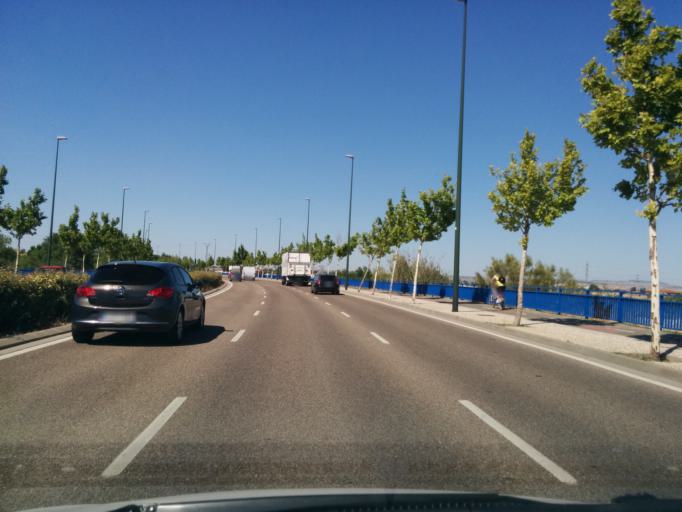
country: ES
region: Aragon
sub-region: Provincia de Zaragoza
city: Zaragoza
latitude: 41.6378
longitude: -0.8596
